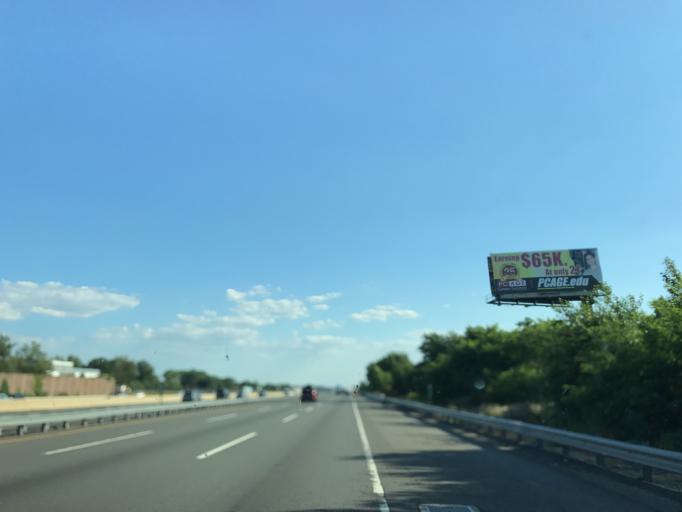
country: US
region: New Jersey
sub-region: Middlesex County
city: Rossmoor
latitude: 40.3424
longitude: -74.4777
